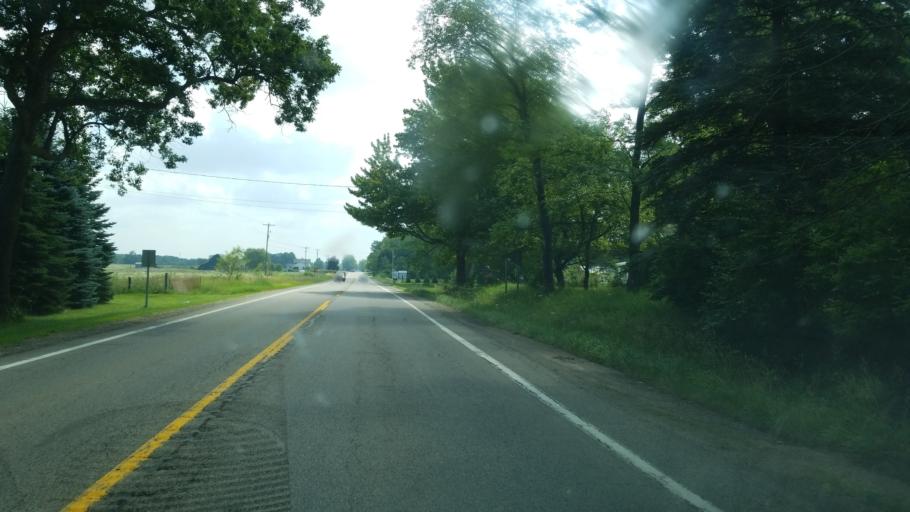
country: US
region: Michigan
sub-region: Kent County
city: Kent City
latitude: 43.2197
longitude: -85.7072
